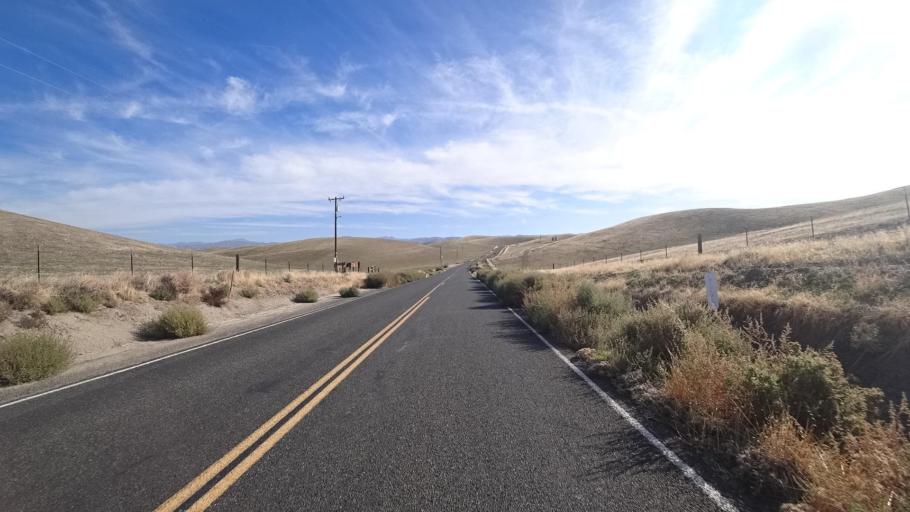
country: US
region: California
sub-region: Kern County
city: Oildale
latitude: 35.6093
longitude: -118.9021
